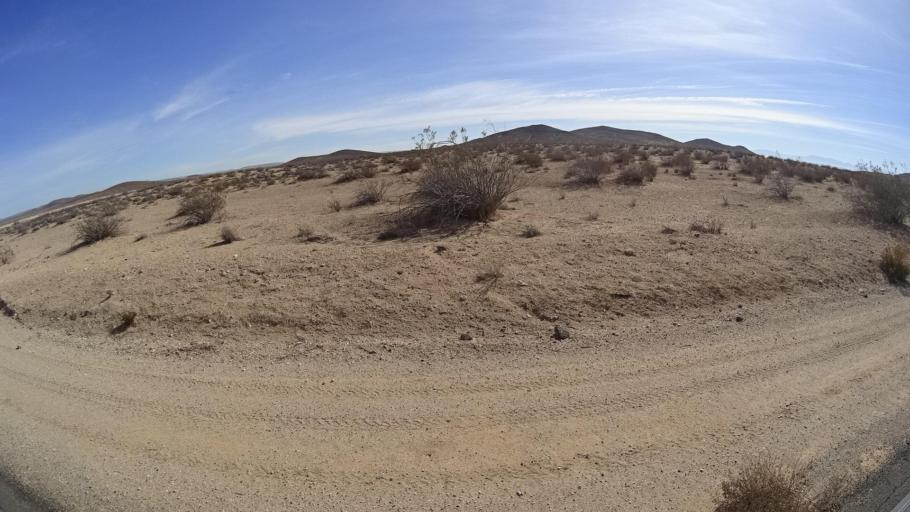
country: US
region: California
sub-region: Kern County
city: North Edwards
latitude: 35.0517
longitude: -117.8153
